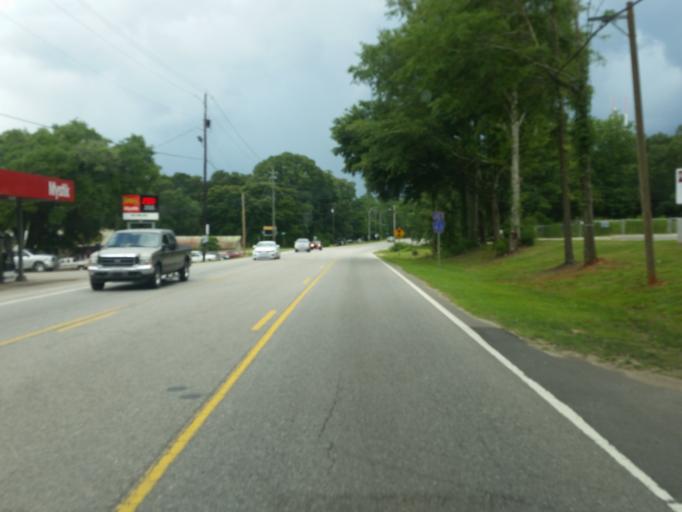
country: US
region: Mississippi
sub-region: Jackson County
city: Hurley
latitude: 30.8233
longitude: -88.3585
